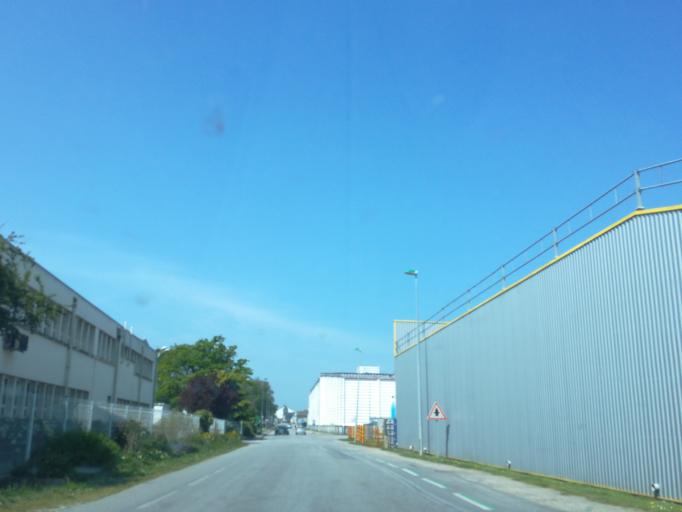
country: FR
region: Brittany
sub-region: Departement du Morbihan
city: Le Sourn
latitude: 48.0482
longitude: -2.9613
